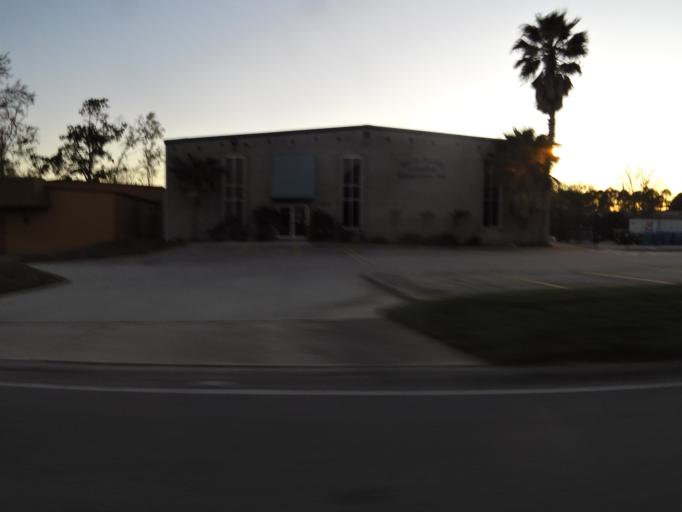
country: US
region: Florida
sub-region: Duval County
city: Jacksonville
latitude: 30.2663
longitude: -81.6241
